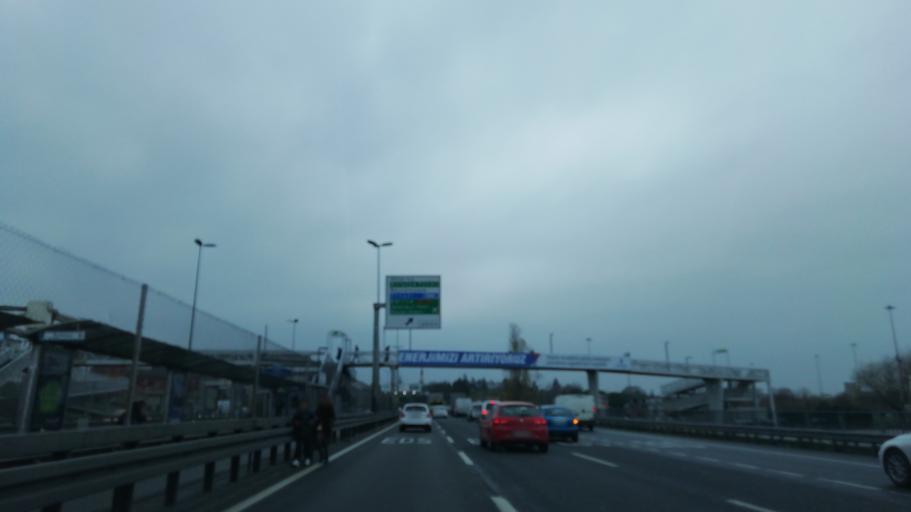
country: TR
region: Istanbul
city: Zeytinburnu
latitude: 41.0201
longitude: 28.9171
